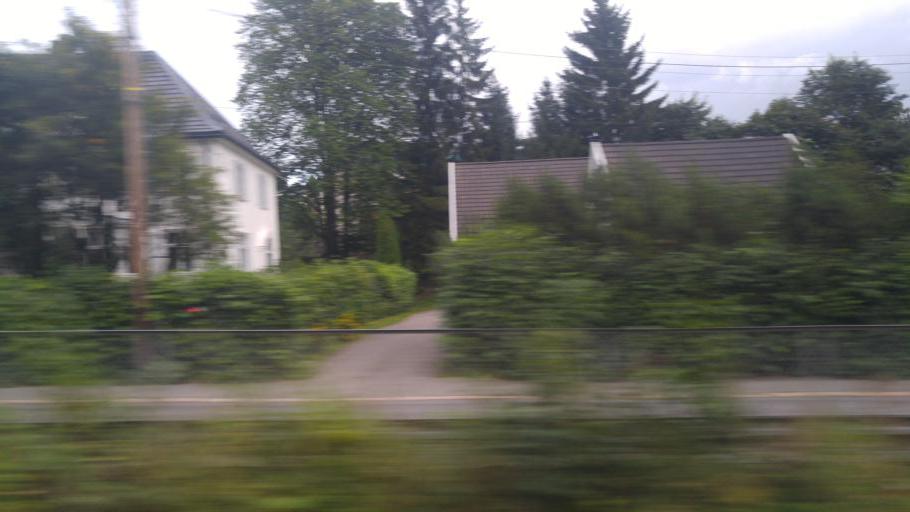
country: NO
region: Oslo
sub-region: Oslo
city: Sjolyststranda
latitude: 59.9415
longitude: 10.7041
